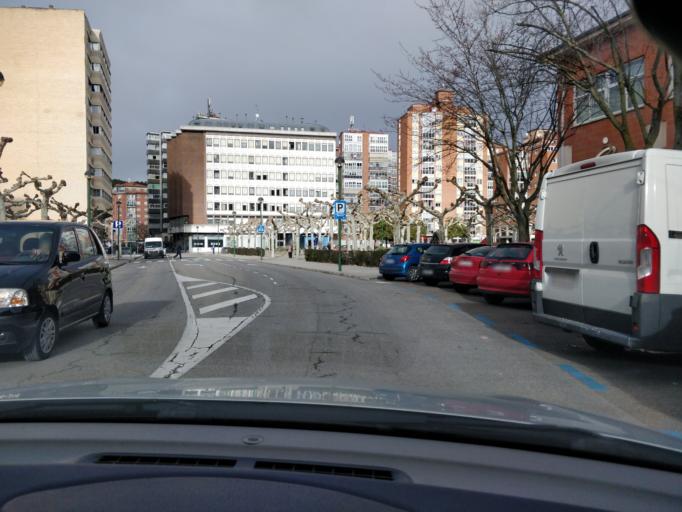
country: ES
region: Castille and Leon
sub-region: Provincia de Burgos
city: Burgos
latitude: 42.3457
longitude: -3.6924
